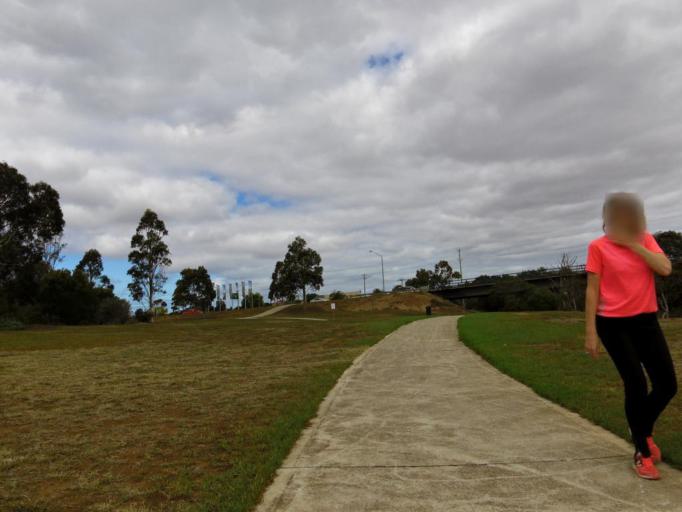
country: AU
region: Victoria
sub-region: Wyndham
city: Werribee
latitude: -37.8868
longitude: 144.6423
